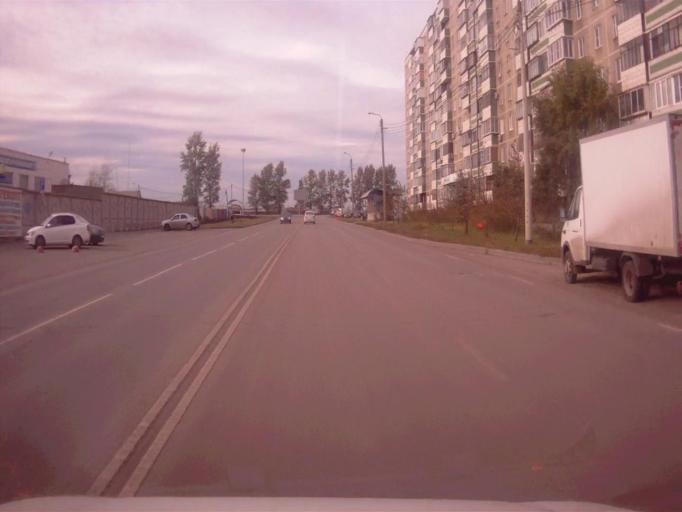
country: RU
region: Chelyabinsk
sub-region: Gorod Chelyabinsk
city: Chelyabinsk
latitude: 55.1177
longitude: 61.4221
